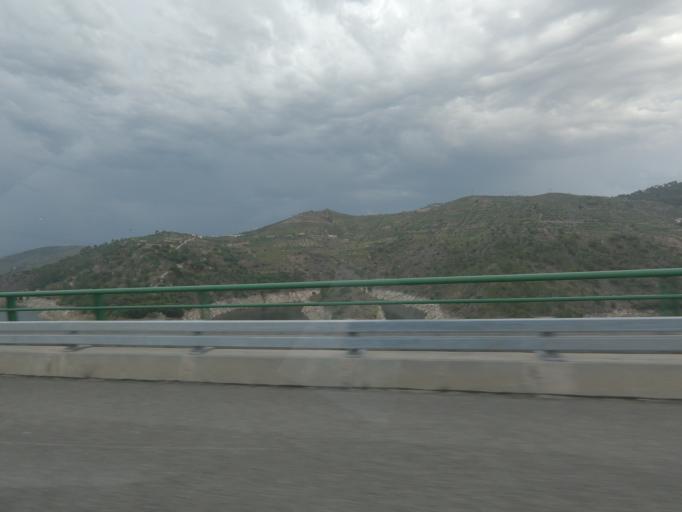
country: PT
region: Viseu
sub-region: Lamego
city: Lamego
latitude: 41.1122
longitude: -7.7772
